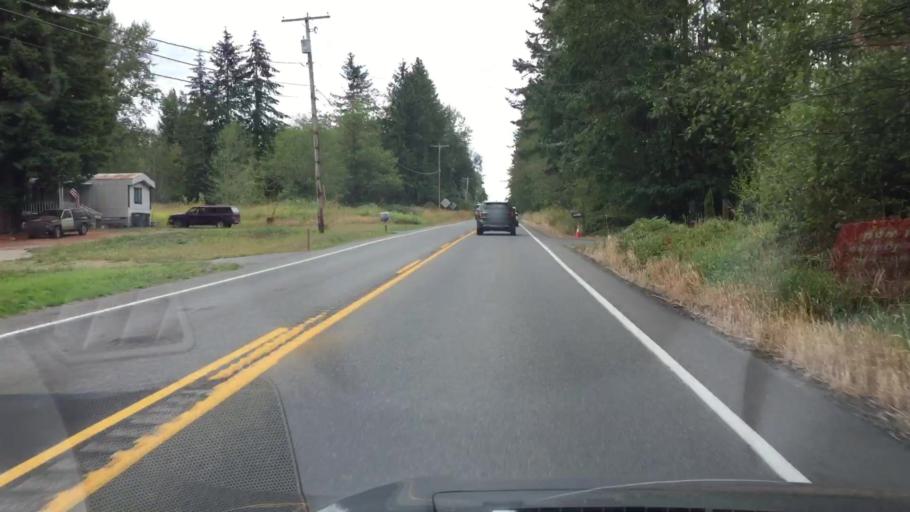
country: US
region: Washington
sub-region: Pierce County
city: Graham
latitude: 46.9641
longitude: -122.2978
